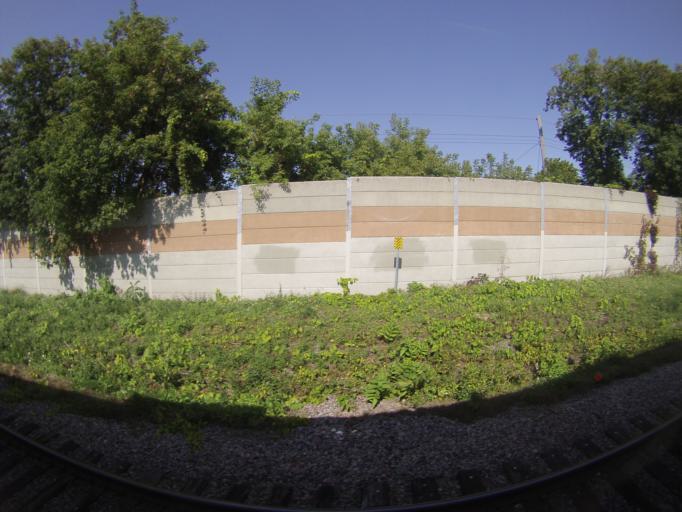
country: CA
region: Ontario
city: Ottawa
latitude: 45.3710
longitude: -75.6702
